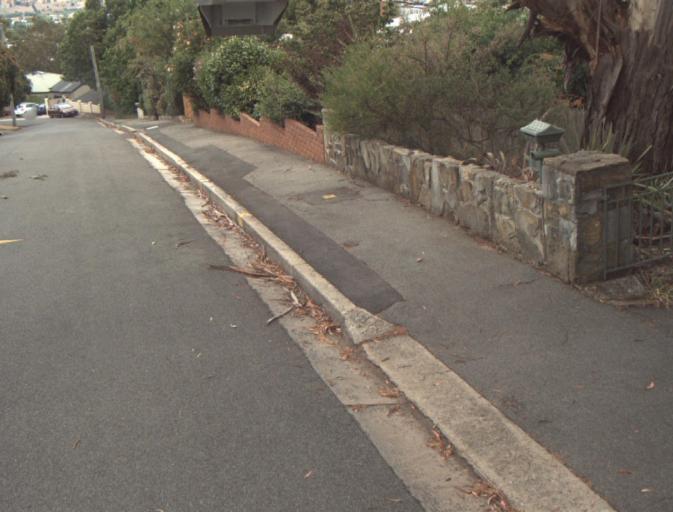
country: AU
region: Tasmania
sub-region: Launceston
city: West Launceston
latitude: -41.4414
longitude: 147.1209
